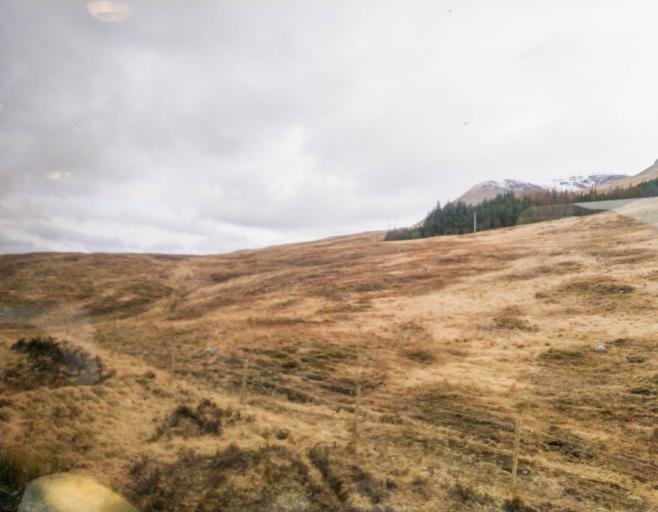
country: GB
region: Scotland
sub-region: Highland
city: Spean Bridge
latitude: 56.5051
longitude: -4.7566
